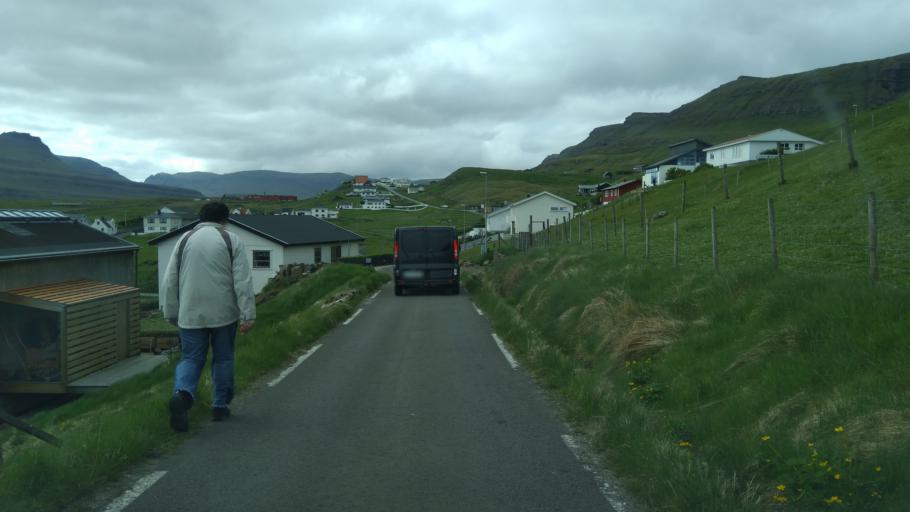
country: FO
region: Suduroy
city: Tvoroyri
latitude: 61.5465
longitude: -6.7716
